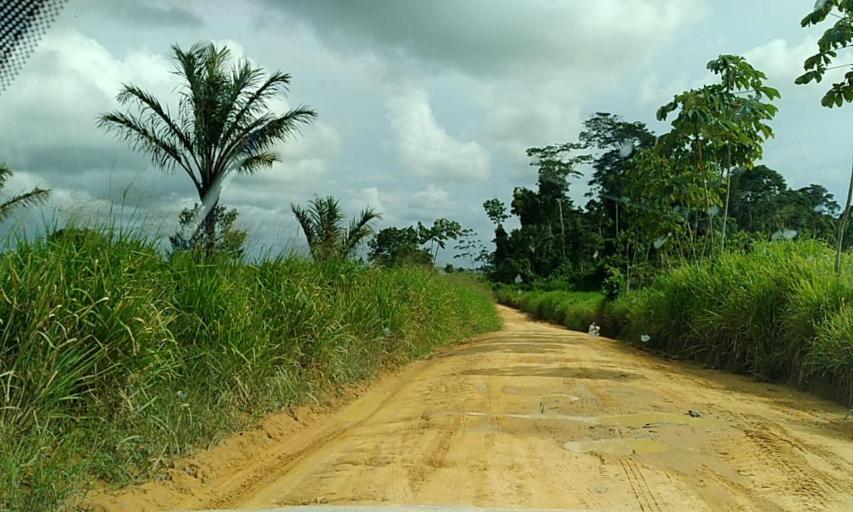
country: BR
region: Para
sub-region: Altamira
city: Altamira
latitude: -3.2370
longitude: -52.6954
